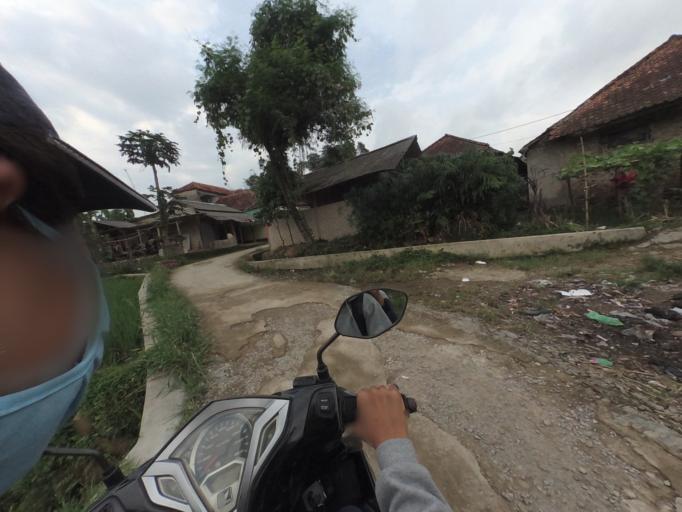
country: ID
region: West Java
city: Ciampea
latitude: -6.6860
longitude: 106.6584
